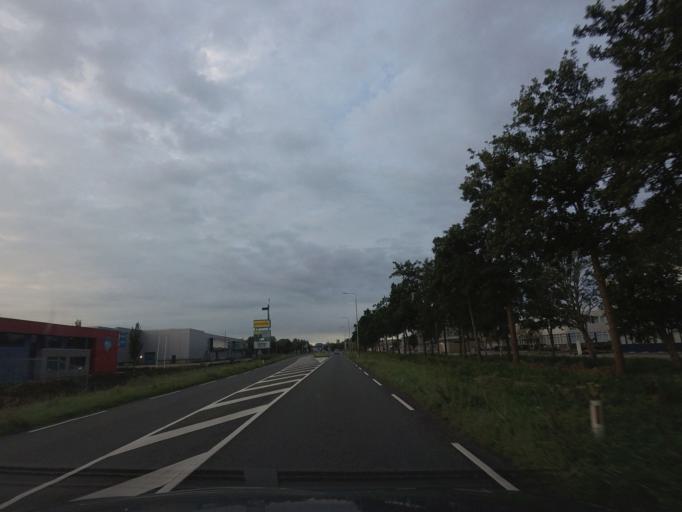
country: NL
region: North Holland
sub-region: Gemeente Zaanstad
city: Zaanstad
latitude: 52.5068
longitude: 4.7793
